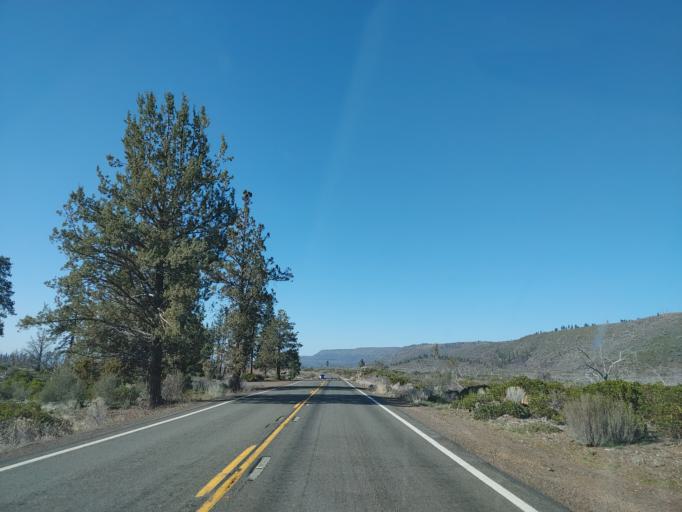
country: US
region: California
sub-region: Shasta County
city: Burney
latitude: 40.7006
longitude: -121.4182
